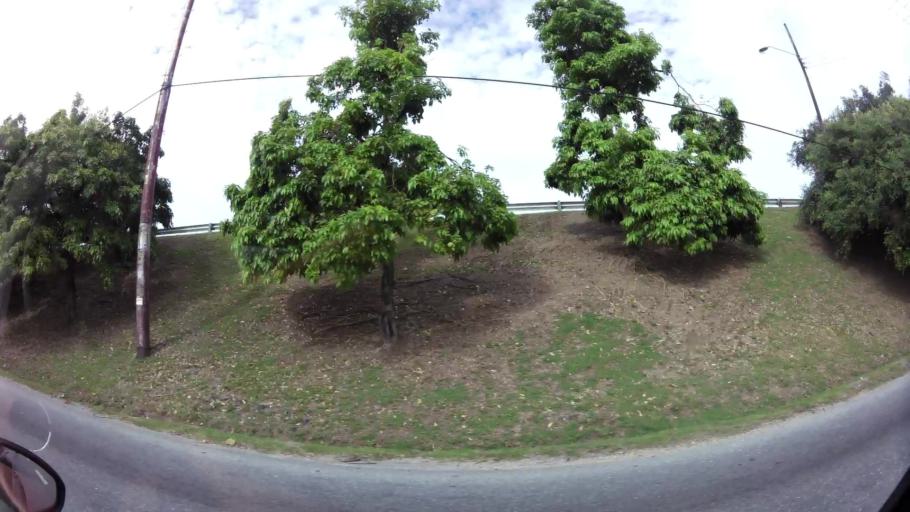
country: TT
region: City of Port of Spain
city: Mucurapo
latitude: 10.6747
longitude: -61.5425
